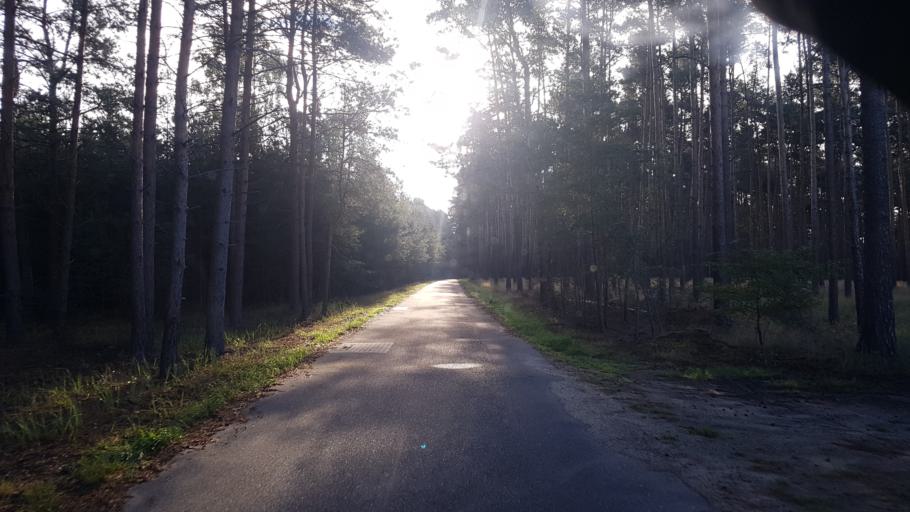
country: DE
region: Brandenburg
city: Bronkow
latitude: 51.6663
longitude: 13.8755
